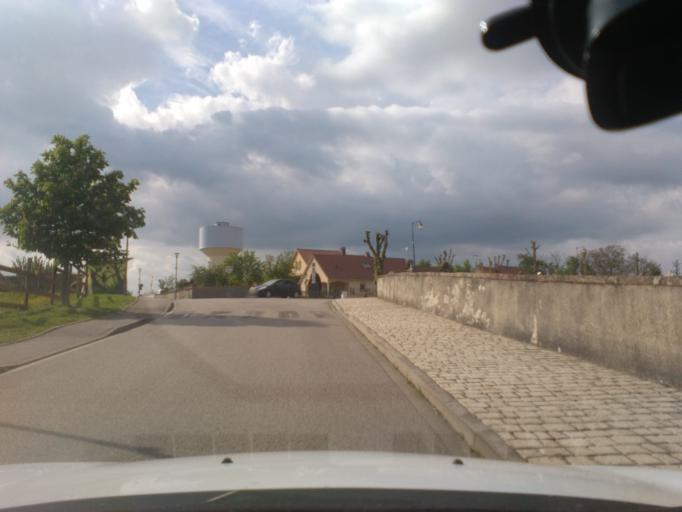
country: FR
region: Lorraine
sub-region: Departement des Vosges
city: Mirecourt
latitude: 48.3175
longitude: 6.1235
